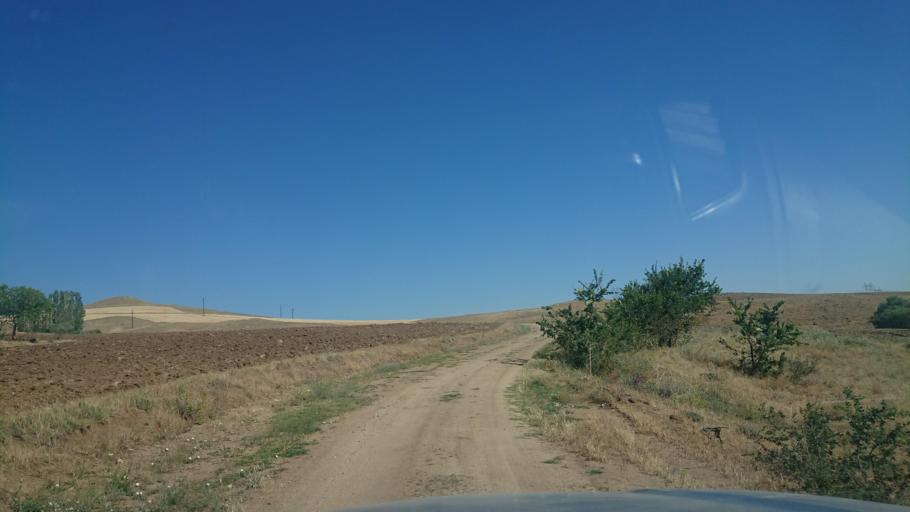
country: TR
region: Aksaray
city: Agacoren
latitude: 38.9089
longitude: 33.8989
